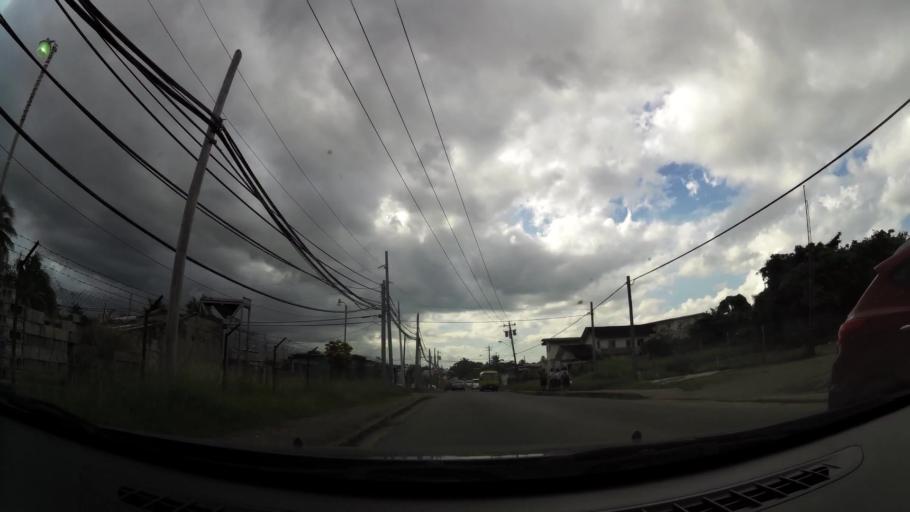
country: TT
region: City of San Fernando
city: Mon Repos
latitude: 10.2672
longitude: -61.4490
